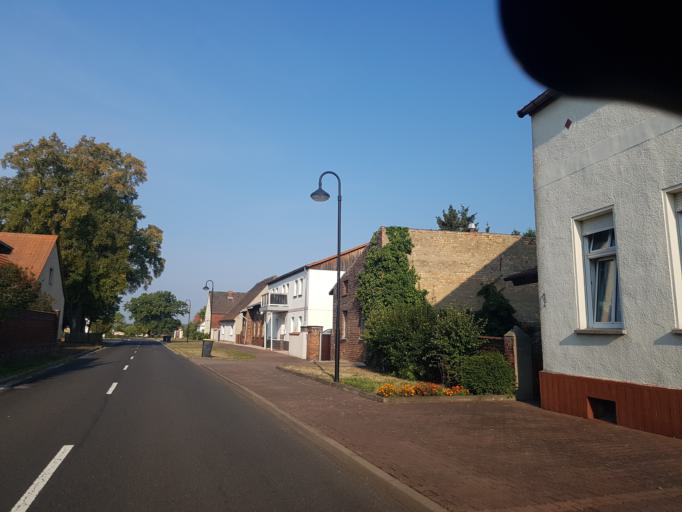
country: DE
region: Saxony-Anhalt
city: Coswig
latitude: 51.9576
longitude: 12.4879
